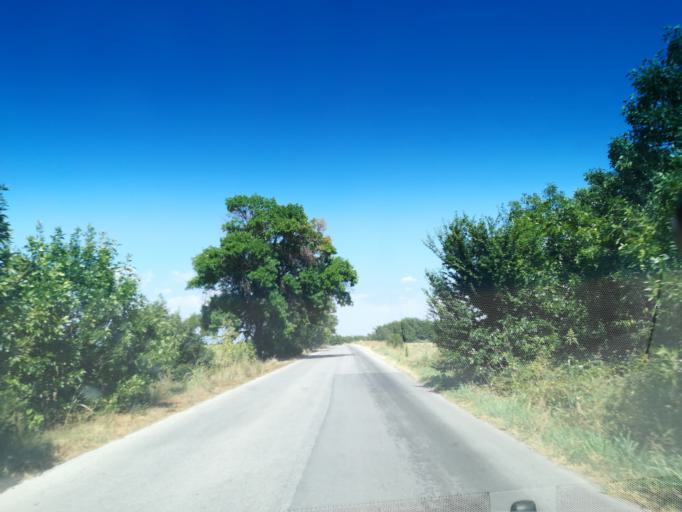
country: BG
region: Stara Zagora
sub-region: Obshtina Chirpan
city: Chirpan
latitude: 42.0656
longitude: 25.1725
